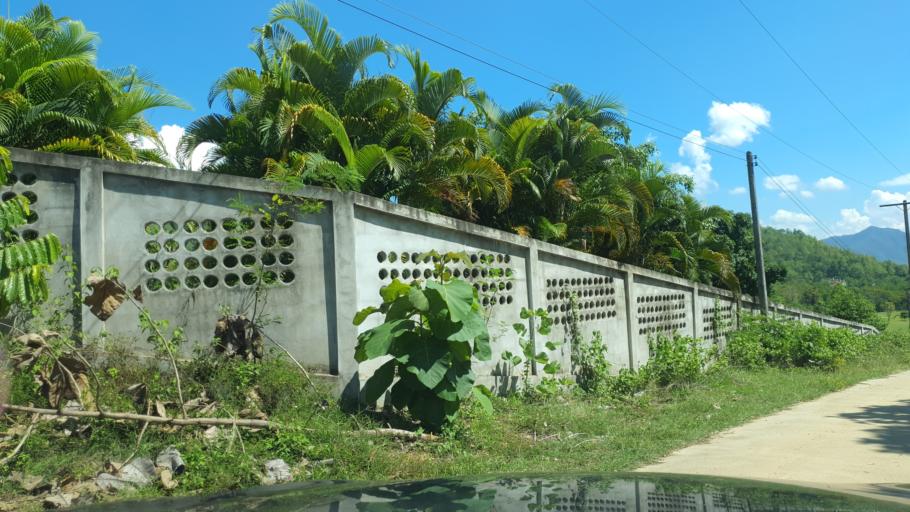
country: TH
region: Chiang Mai
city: Mae On
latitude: 18.8033
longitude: 99.2690
